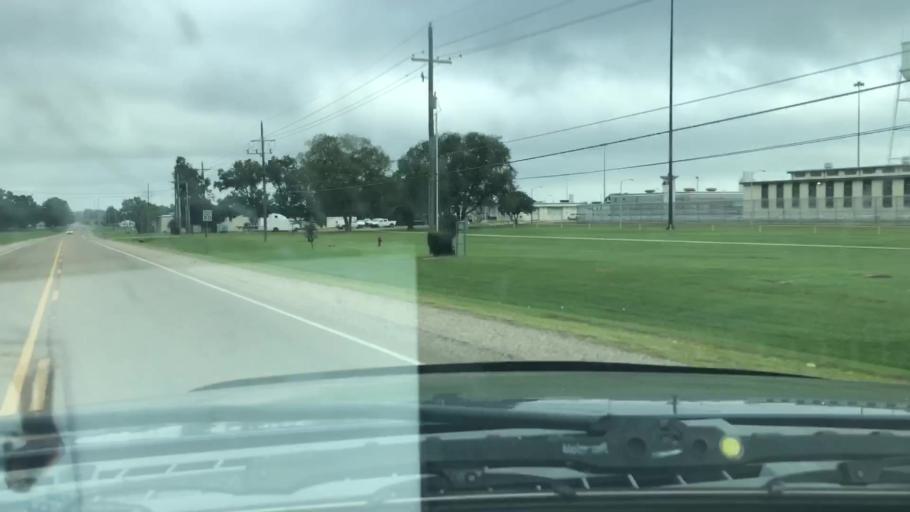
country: US
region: Texas
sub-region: Bowie County
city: Wake Village
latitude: 33.3760
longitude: -94.0921
